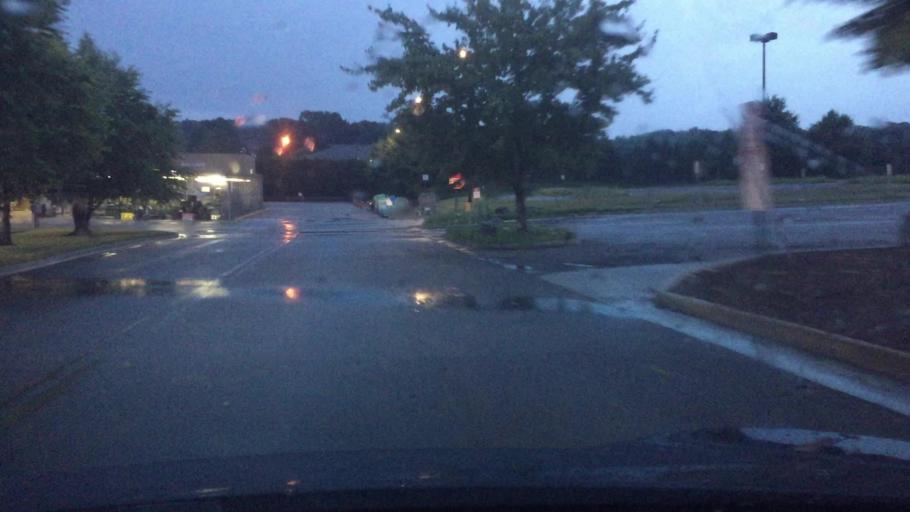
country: US
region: Virginia
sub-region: Wythe County
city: Wytheville
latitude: 36.9571
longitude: -81.1006
